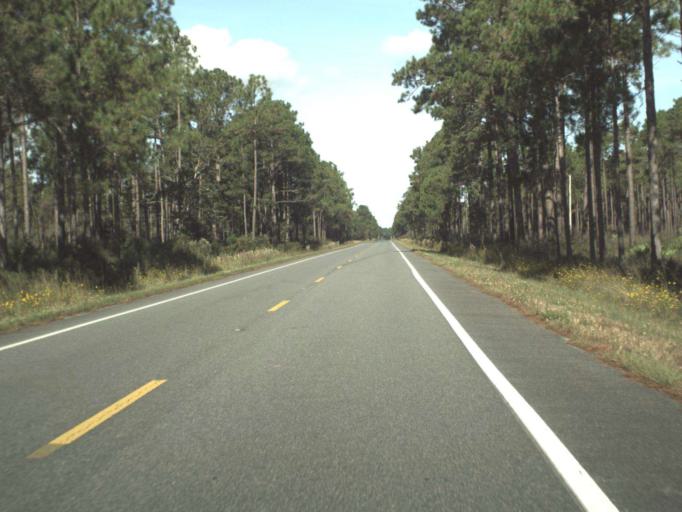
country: US
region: Florida
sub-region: Franklin County
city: Eastpoint
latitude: 29.8081
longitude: -84.8390
